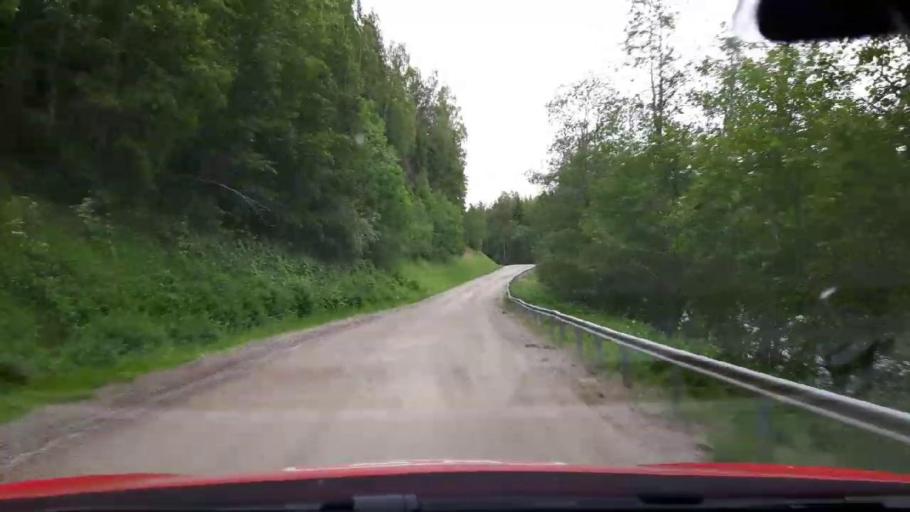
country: SE
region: Jaemtland
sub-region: Ragunda Kommun
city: Hammarstrand
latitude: 63.1965
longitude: 16.1338
